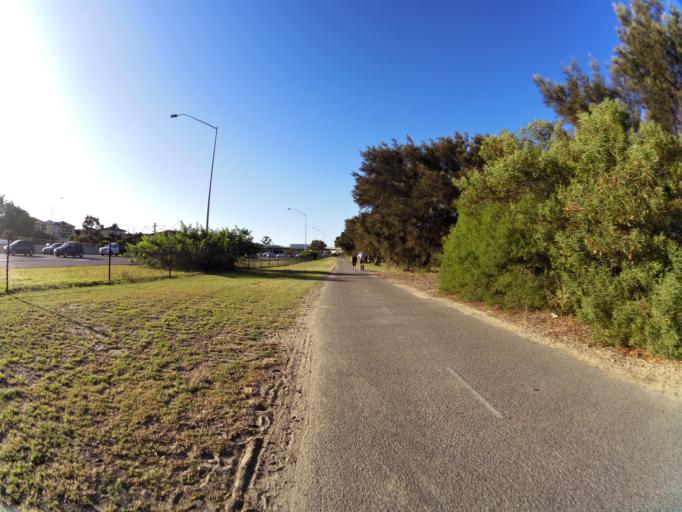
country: AU
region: Western Australia
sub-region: South Perth
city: Manning
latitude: -32.0155
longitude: 115.8572
